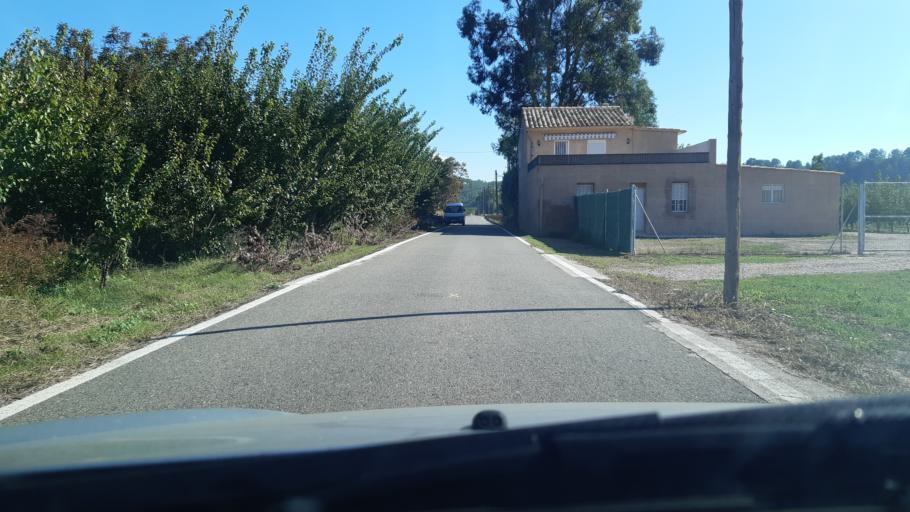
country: ES
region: Catalonia
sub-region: Provincia de Tarragona
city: Miravet
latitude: 41.0353
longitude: 0.6026
